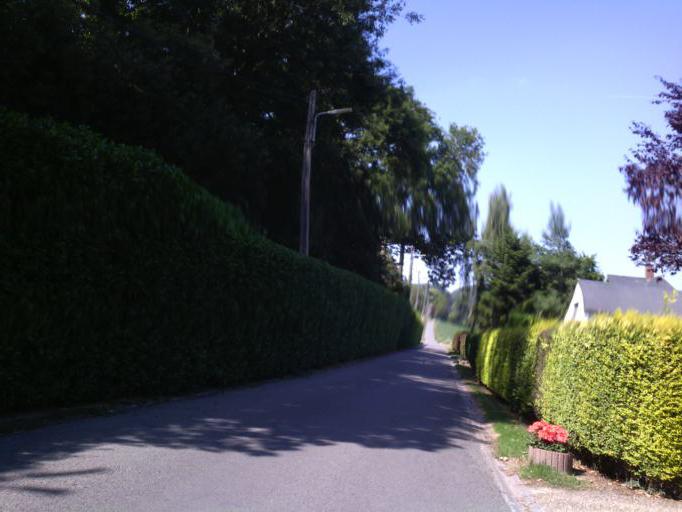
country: BE
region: Wallonia
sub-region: Province du Hainaut
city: Tournai
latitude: 50.6401
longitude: 3.3934
